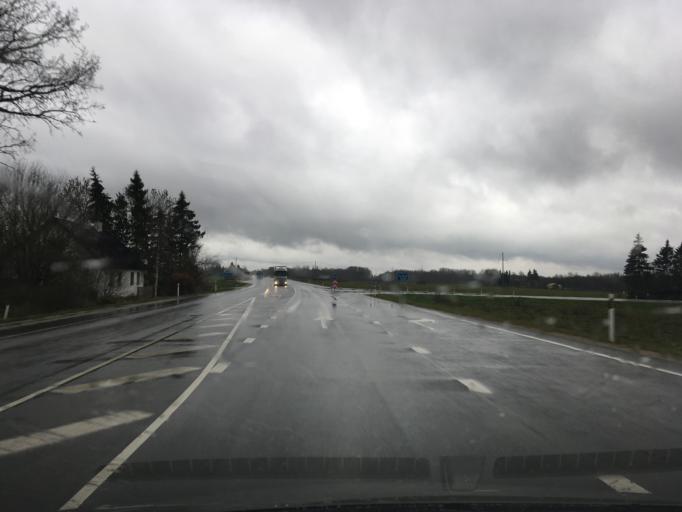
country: EE
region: Laeaene
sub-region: Lihula vald
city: Lihula
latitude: 58.7669
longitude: 23.9882
